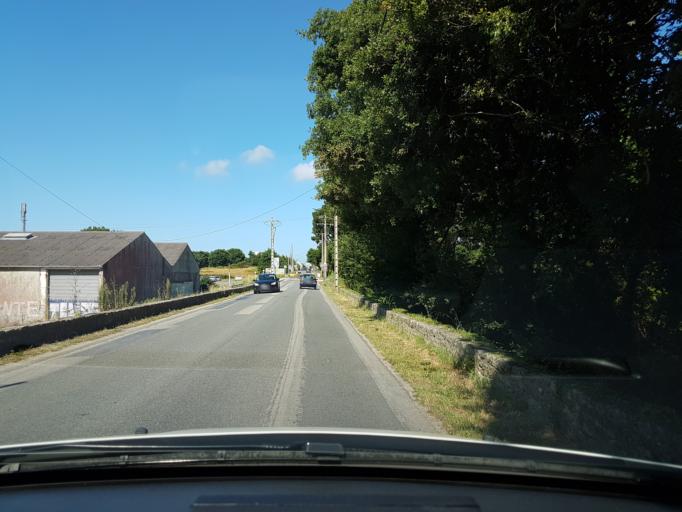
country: FR
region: Brittany
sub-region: Departement du Morbihan
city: Belz
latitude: 47.6758
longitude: -3.1854
